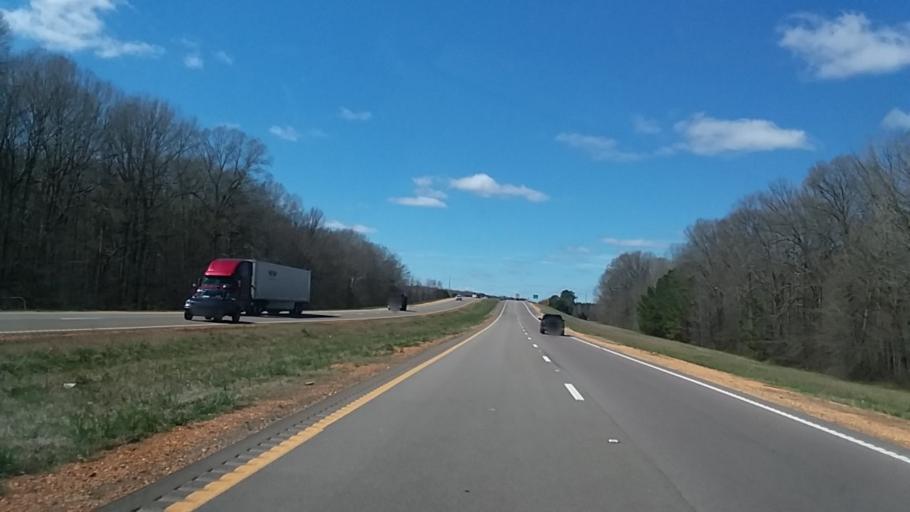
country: US
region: Mississippi
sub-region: Tishomingo County
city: Iuka
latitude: 34.8247
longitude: -88.2976
